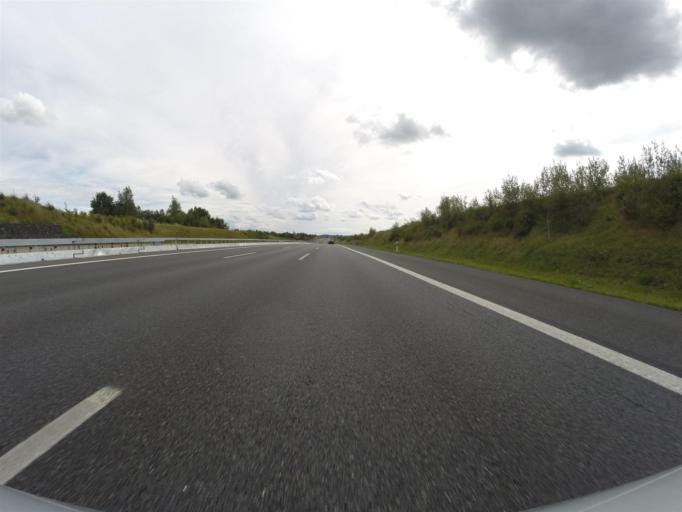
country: DE
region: Bavaria
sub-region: Upper Franconia
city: Bayreuth
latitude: 49.9476
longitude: 11.6069
